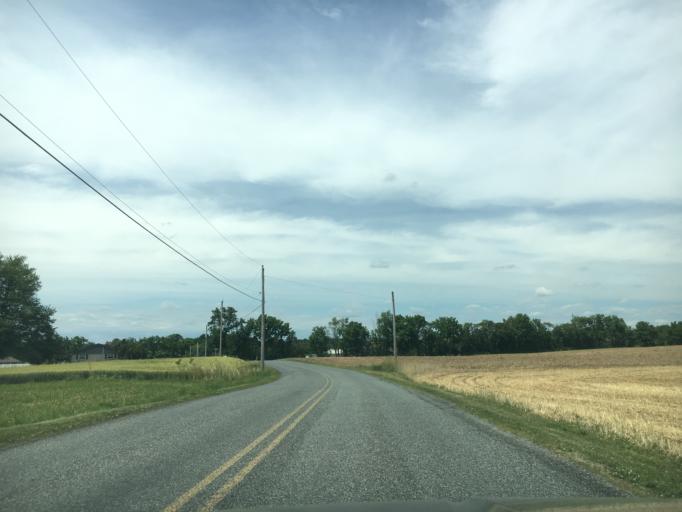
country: US
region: Pennsylvania
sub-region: Berks County
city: Kutztown
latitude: 40.4978
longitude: -75.7885
